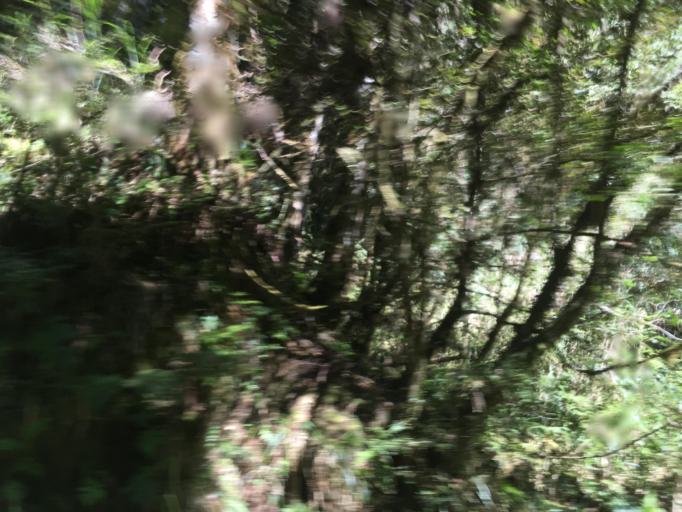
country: TW
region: Taiwan
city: Daxi
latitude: 24.5901
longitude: 121.4110
